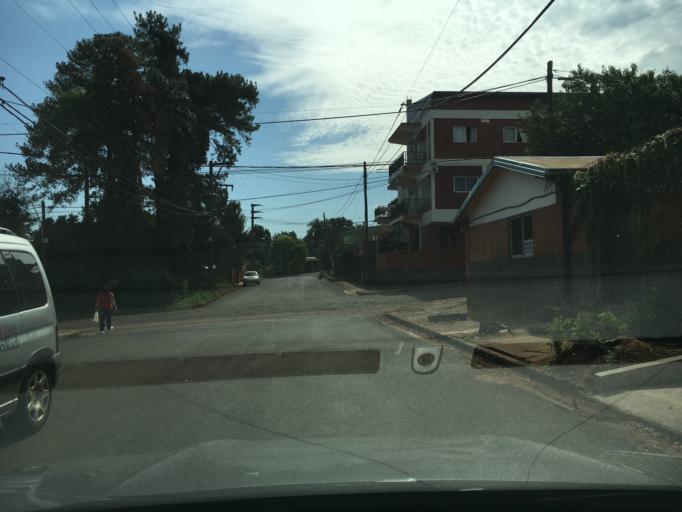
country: AR
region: Misiones
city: Puerto Rico
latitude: -26.8101
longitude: -55.0282
